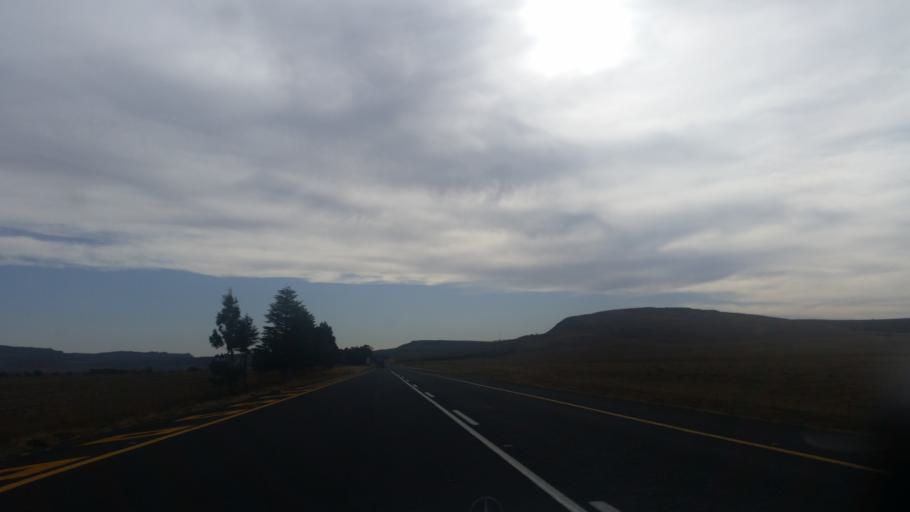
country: ZA
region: Orange Free State
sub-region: Thabo Mofutsanyana District Municipality
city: Phuthaditjhaba
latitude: -28.3130
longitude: 28.7371
